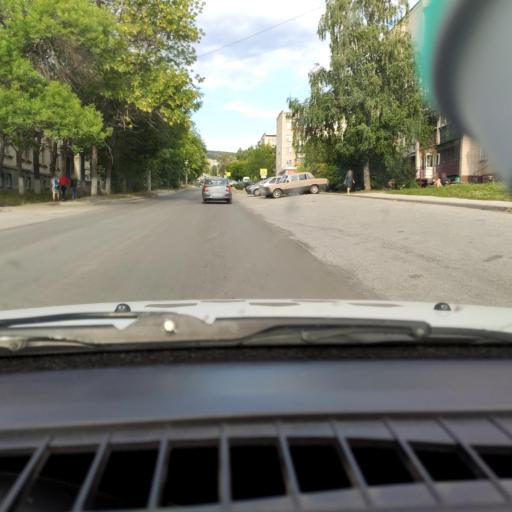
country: RU
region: Chelyabinsk
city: Miass
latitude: 55.0612
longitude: 60.1127
